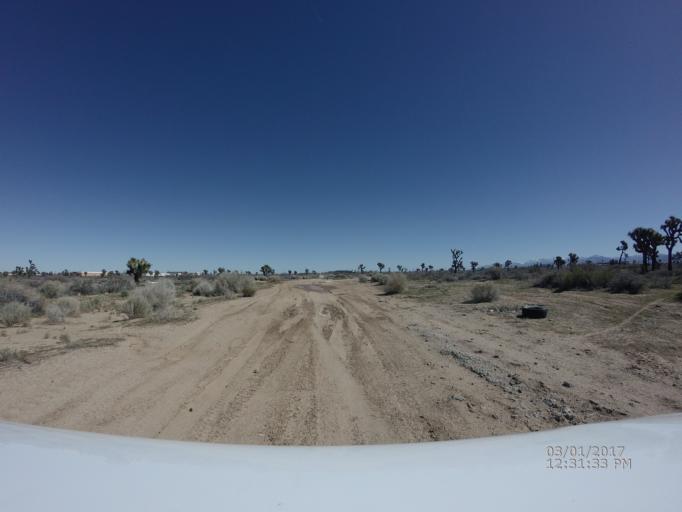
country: US
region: California
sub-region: Los Angeles County
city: Desert View Highlands
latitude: 34.6385
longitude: -118.1572
